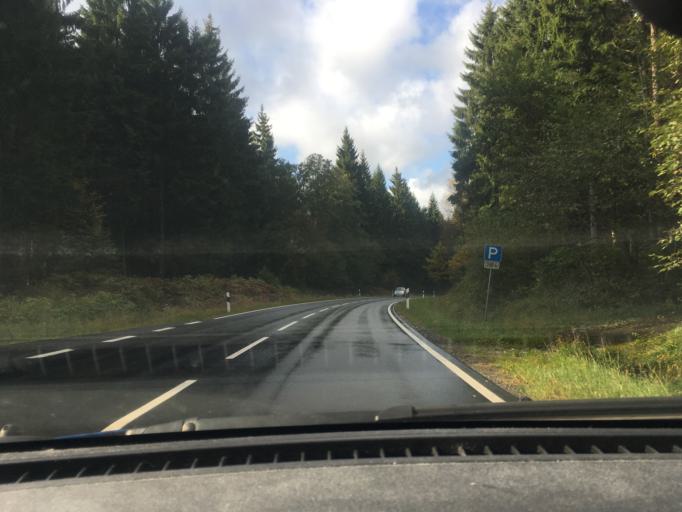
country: DE
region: Lower Saxony
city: Bevern
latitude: 51.7782
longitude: 9.5239
